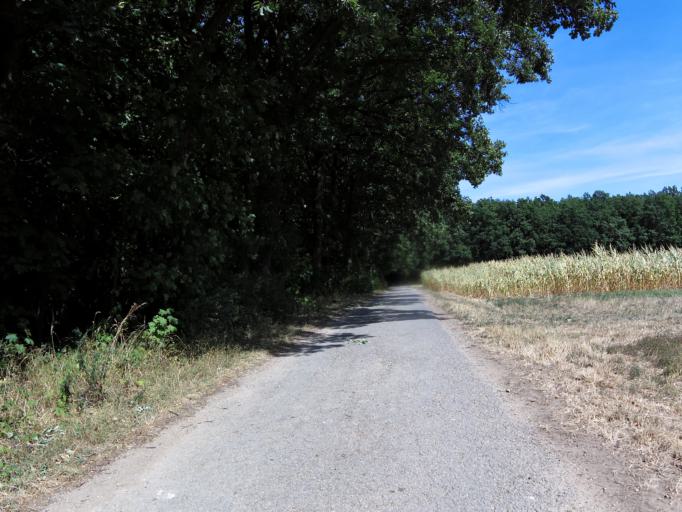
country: DE
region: Bavaria
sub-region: Regierungsbezirk Unterfranken
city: Theilheim
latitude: 49.7485
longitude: 10.0138
